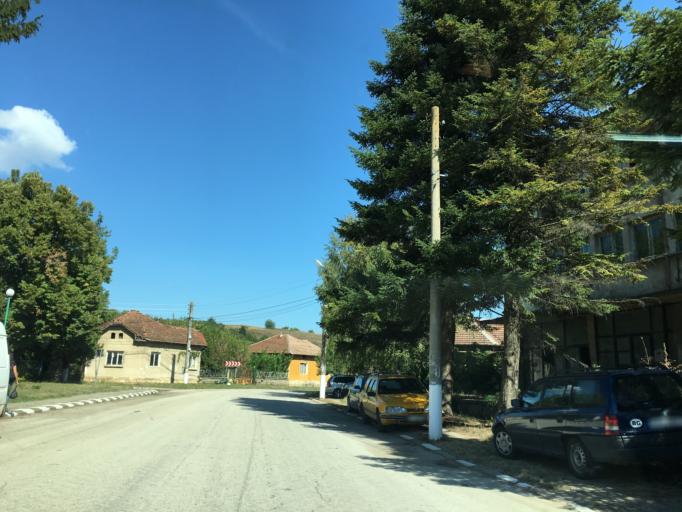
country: RO
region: Olt
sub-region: Comuna Orlea
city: Orlea
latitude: 43.6480
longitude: 24.4008
